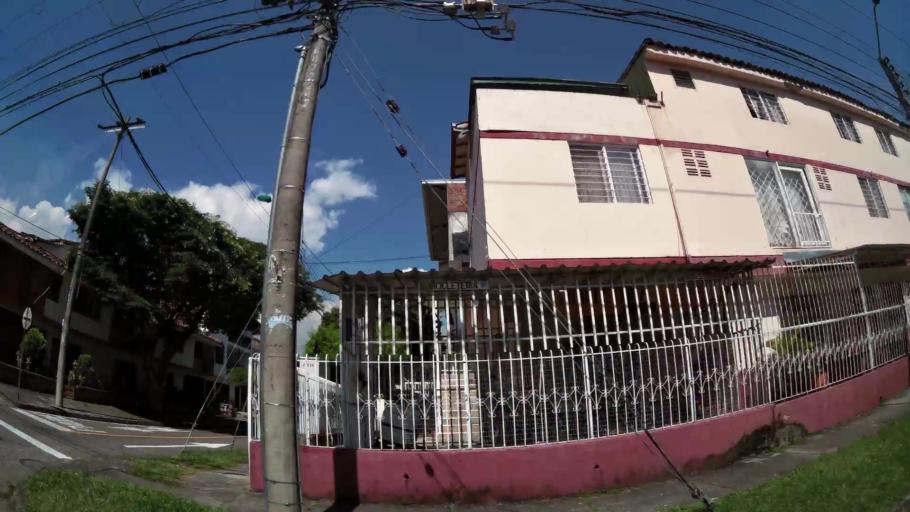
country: CO
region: Valle del Cauca
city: Cali
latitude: 3.4258
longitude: -76.5312
